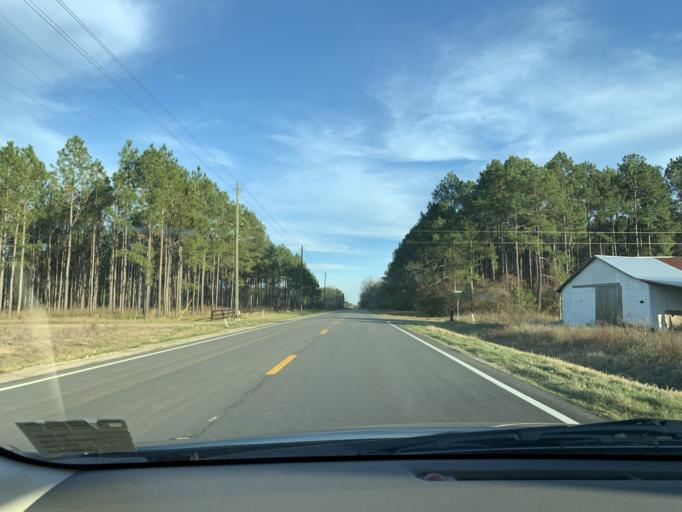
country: US
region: Georgia
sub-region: Irwin County
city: Ocilla
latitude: 31.5842
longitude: -83.0735
